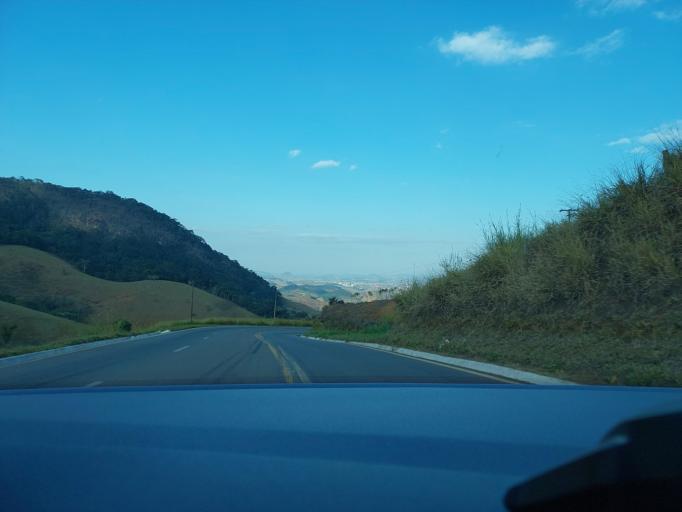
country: BR
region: Minas Gerais
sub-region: Muriae
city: Muriae
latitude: -21.0797
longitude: -42.4941
